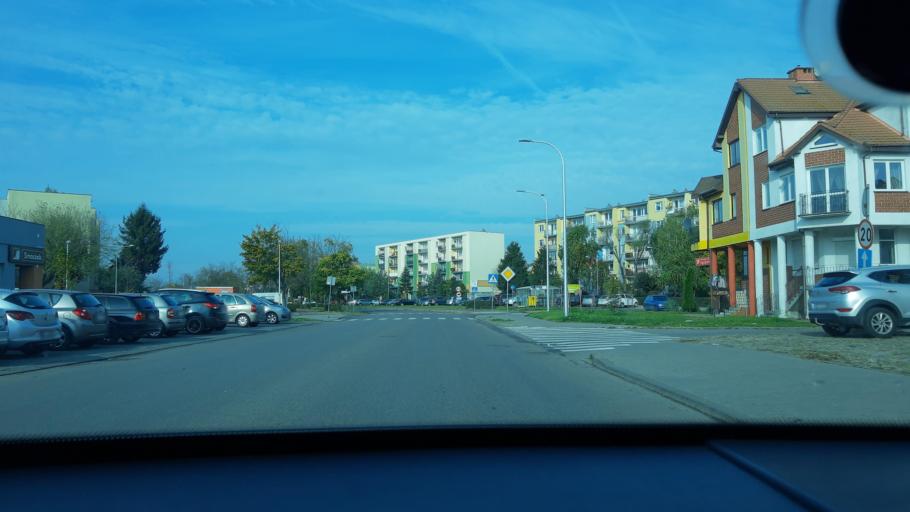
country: PL
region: Lodz Voivodeship
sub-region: Powiat sieradzki
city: Sieradz
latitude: 51.5888
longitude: 18.7109
